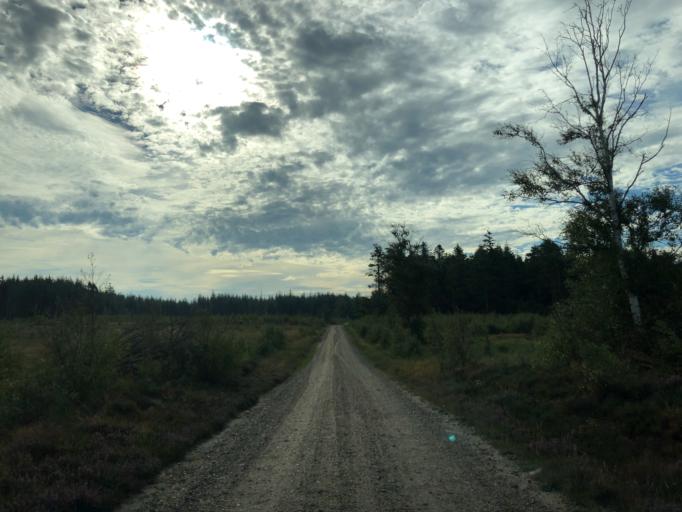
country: DK
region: Central Jutland
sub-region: Holstebro Kommune
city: Ulfborg
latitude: 56.1705
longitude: 8.3825
